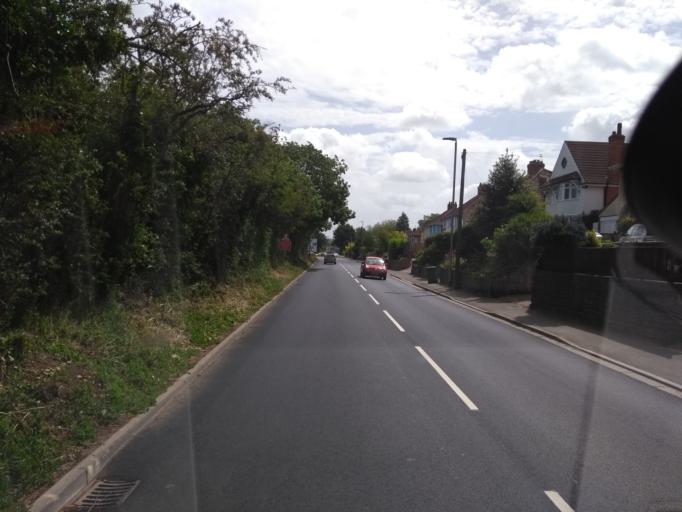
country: GB
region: England
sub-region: Somerset
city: Bridgwater
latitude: 51.1285
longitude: -3.0275
